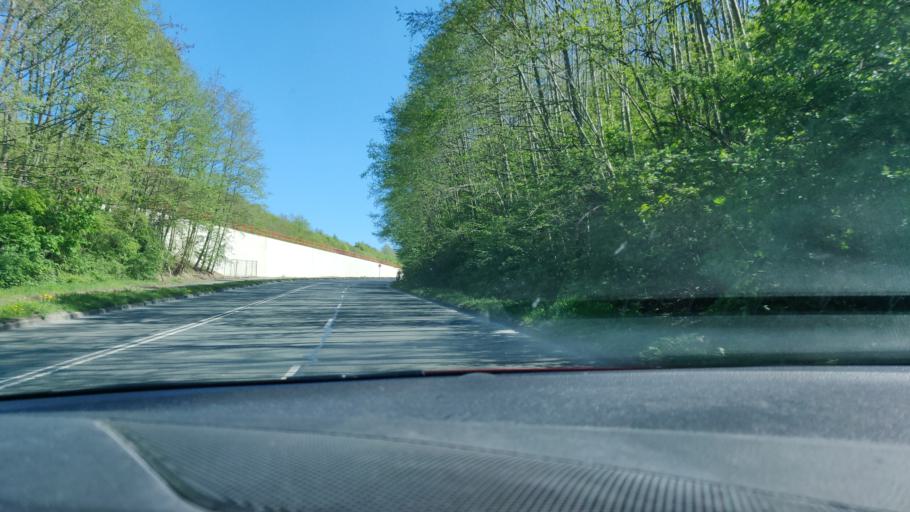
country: DE
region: North Rhine-Westphalia
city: Wulfrath
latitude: 51.2512
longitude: 7.0490
